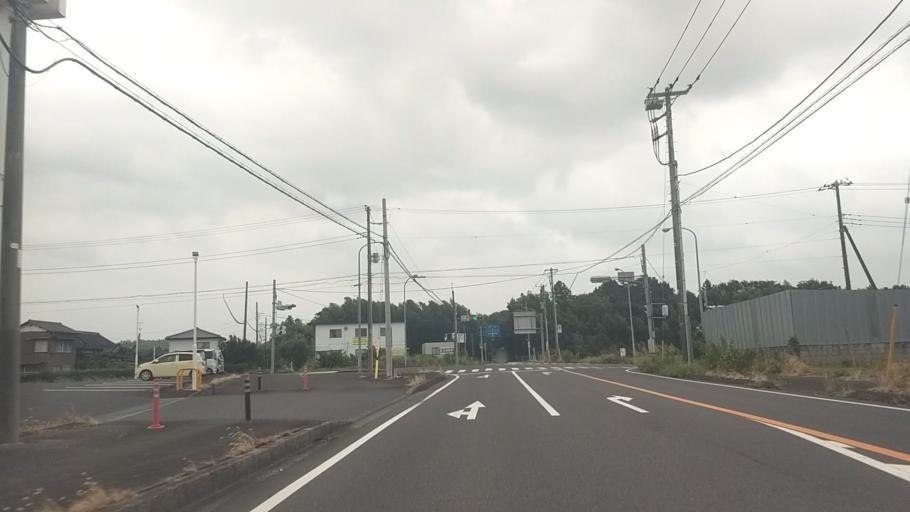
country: JP
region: Chiba
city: Ichihara
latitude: 35.3882
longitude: 140.0568
